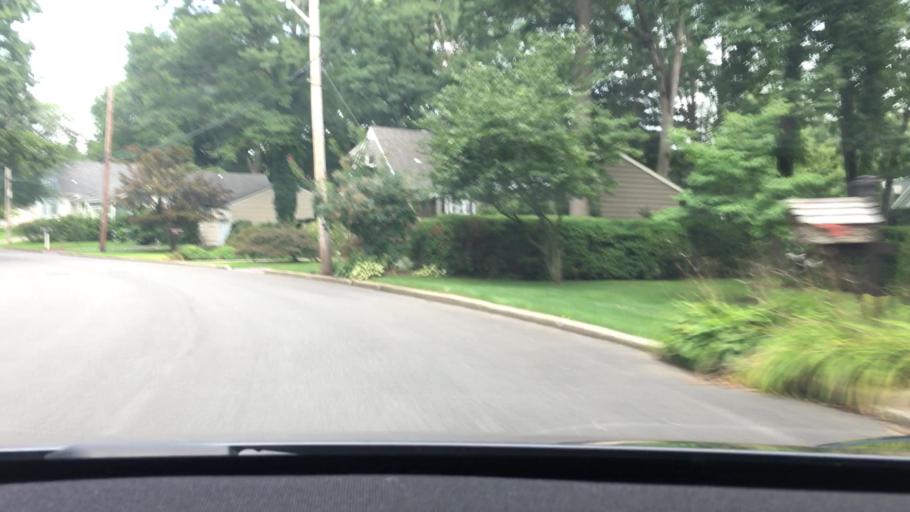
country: US
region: New York
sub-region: Westchester County
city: Larchmont
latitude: 40.9470
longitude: -73.7754
